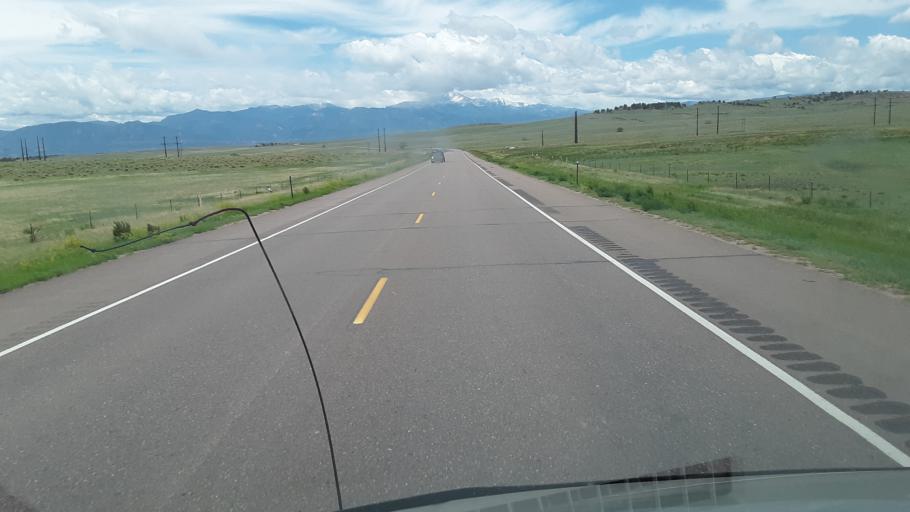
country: US
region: Colorado
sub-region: El Paso County
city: Cimarron Hills
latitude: 38.8389
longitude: -104.6175
